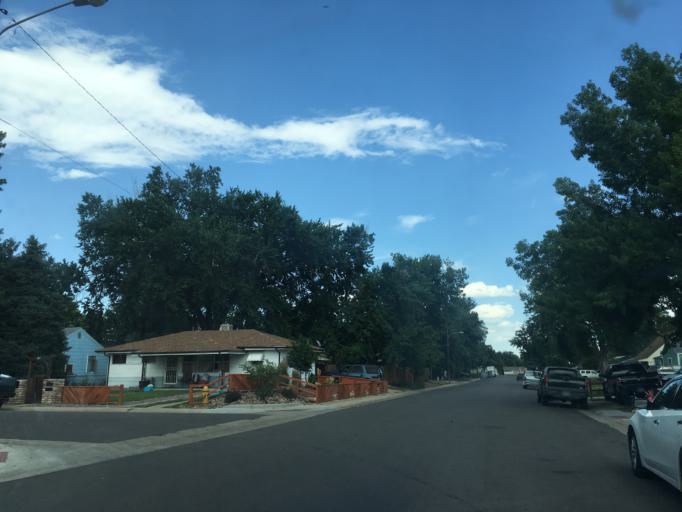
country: US
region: Colorado
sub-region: Jefferson County
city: Lakewood
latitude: 39.6862
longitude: -105.0524
